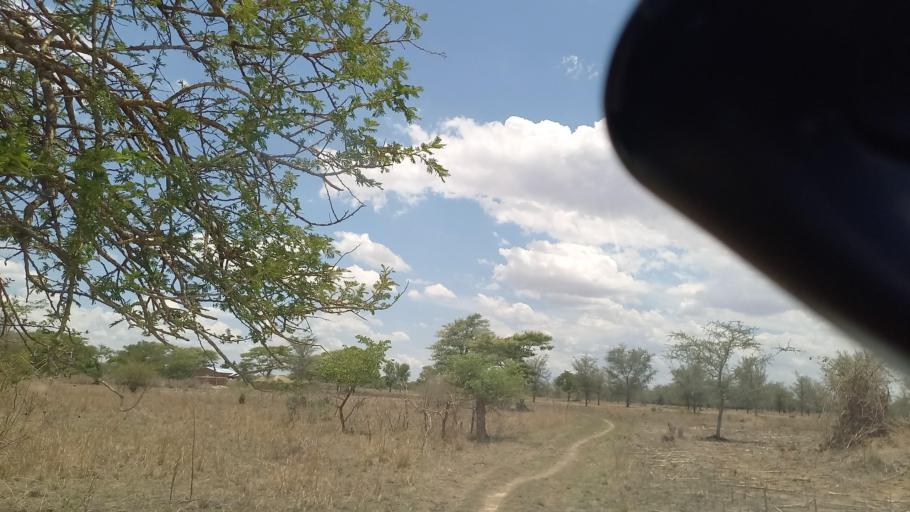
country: ZM
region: Southern
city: Mazabuka
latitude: -16.1245
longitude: 27.7788
